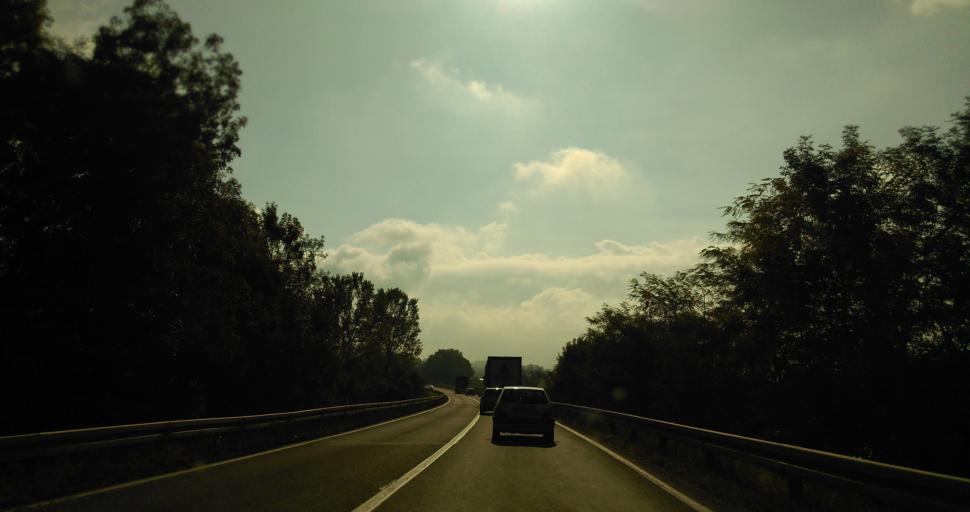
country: RS
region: Central Serbia
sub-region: Kolubarski Okrug
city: Lajkovac
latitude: 44.3456
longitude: 20.1982
